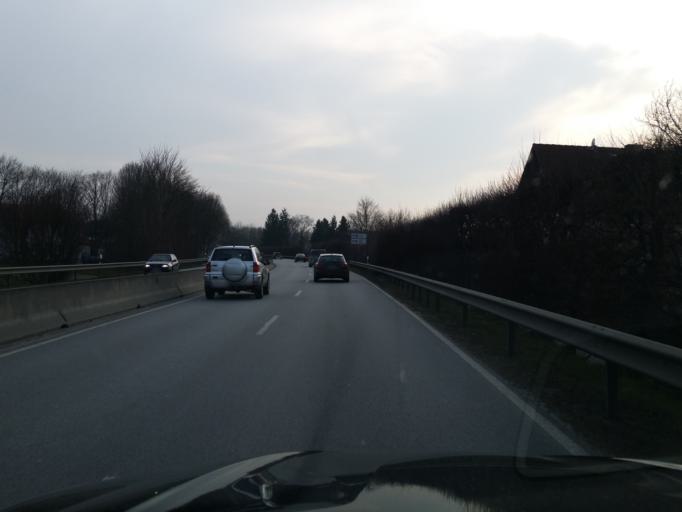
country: DE
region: Bavaria
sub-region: Lower Bavaria
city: Ergolding
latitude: 48.5580
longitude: 12.1639
